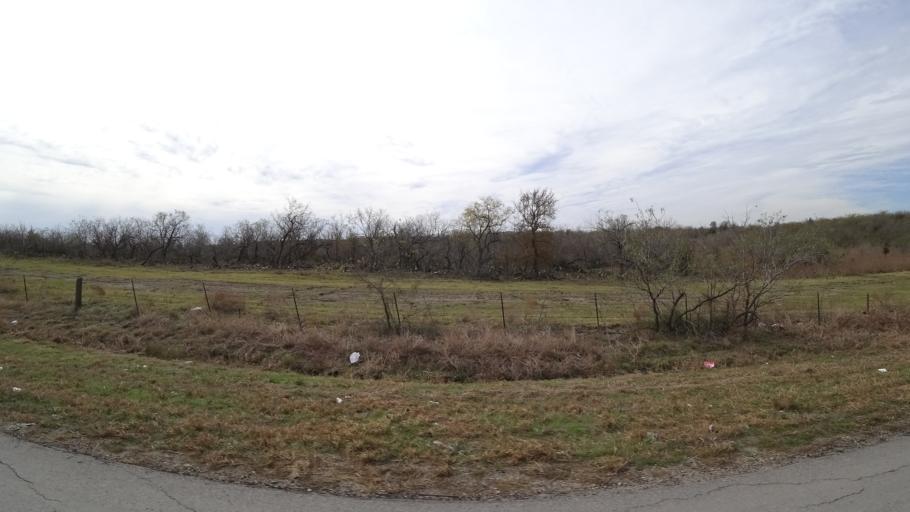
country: US
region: Texas
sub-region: Travis County
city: Garfield
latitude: 30.1592
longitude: -97.6017
